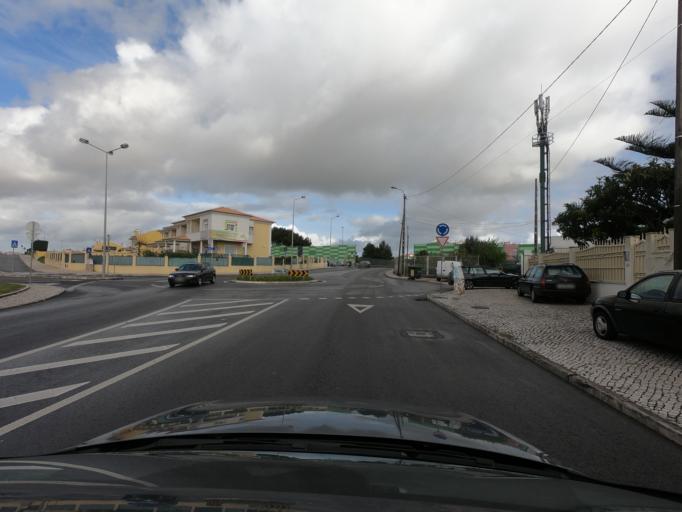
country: PT
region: Lisbon
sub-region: Cascais
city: Sao Domingos de Rana
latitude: 38.7071
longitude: -9.3268
